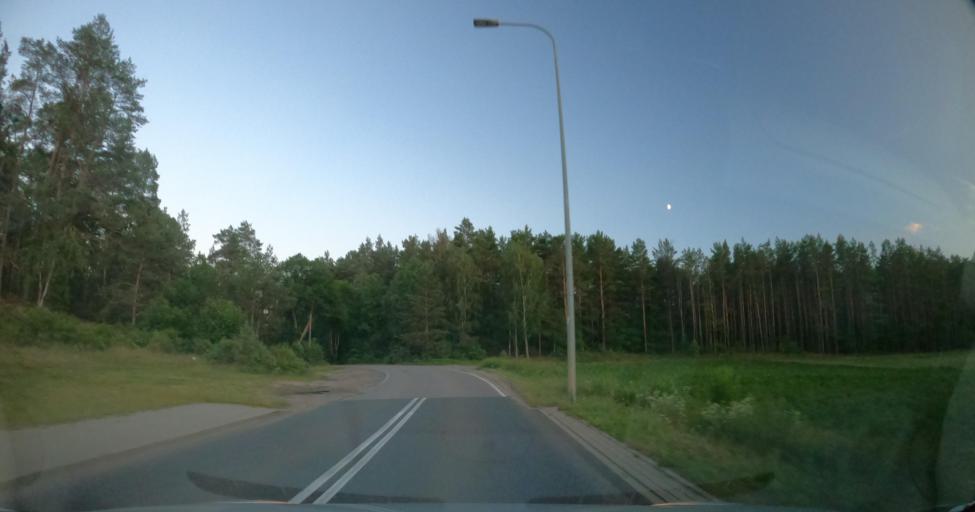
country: PL
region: Pomeranian Voivodeship
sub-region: Powiat wejherowski
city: Luzino
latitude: 54.4748
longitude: 18.0908
